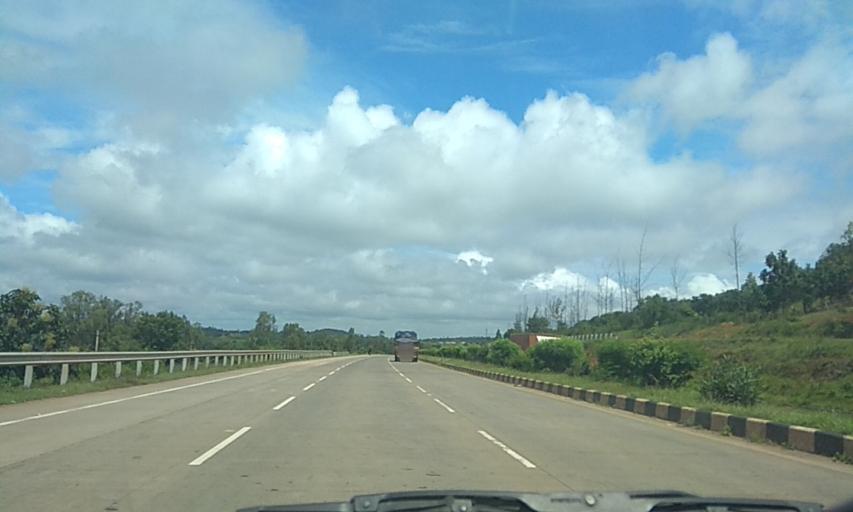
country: IN
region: Karnataka
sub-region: Dharwad
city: Alnavar
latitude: 15.6164
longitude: 74.7617
